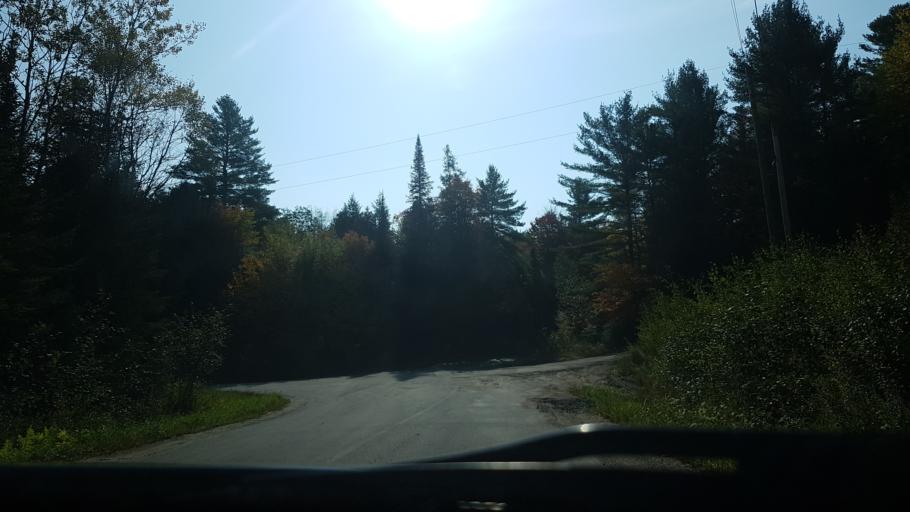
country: CA
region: Ontario
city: Bracebridge
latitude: 44.9494
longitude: -79.2447
